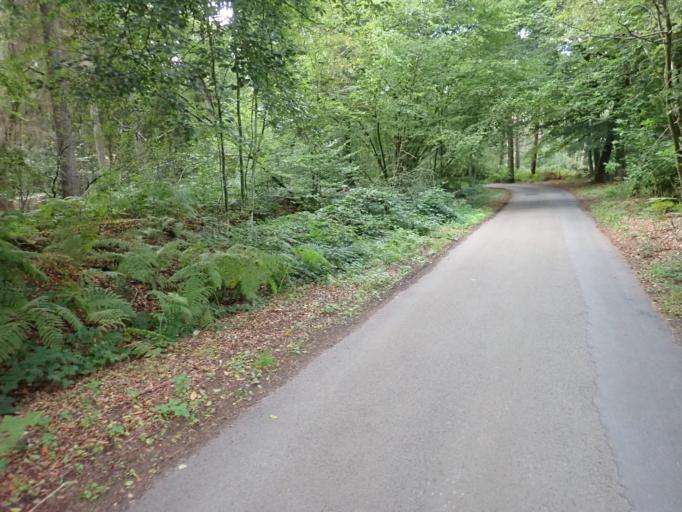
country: BE
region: Flanders
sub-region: Provincie Antwerpen
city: Oostmalle
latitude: 51.2874
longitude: 4.7662
